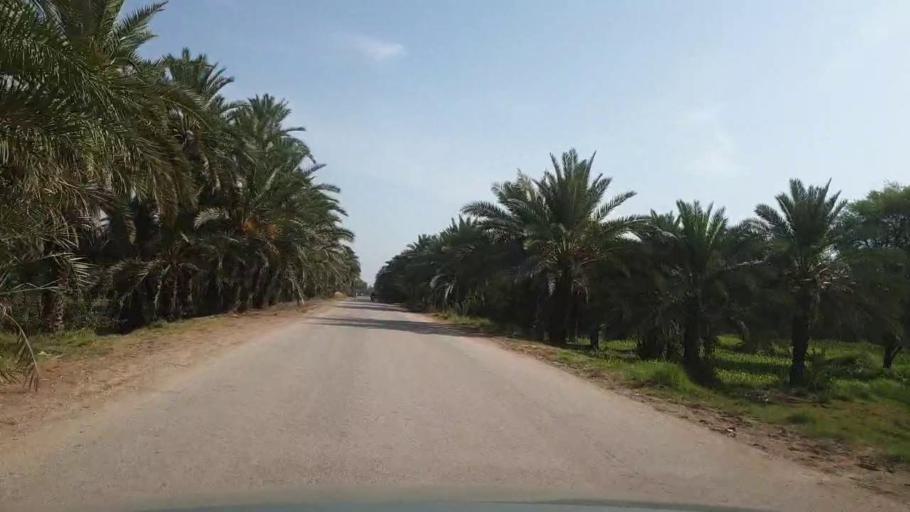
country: PK
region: Sindh
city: Rohri
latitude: 27.6695
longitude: 68.8786
